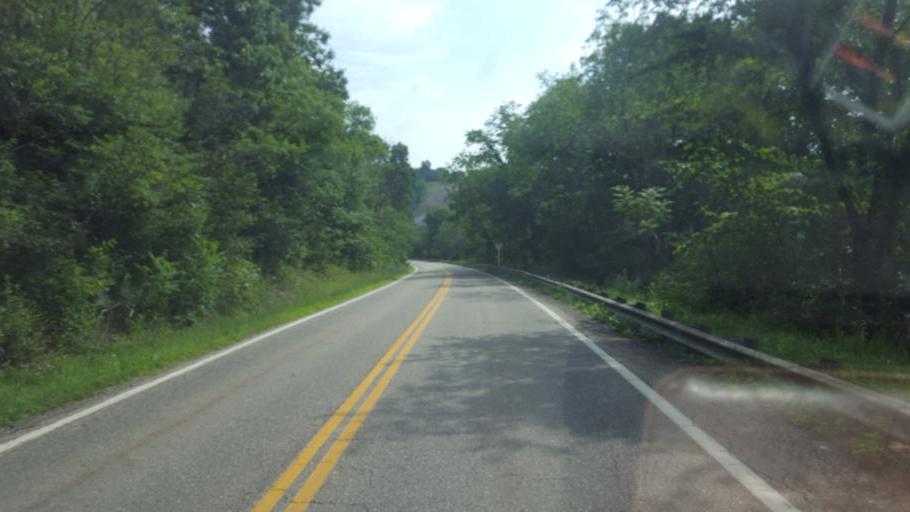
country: US
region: Ohio
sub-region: Columbiana County
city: Salineville
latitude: 40.6226
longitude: -80.8209
